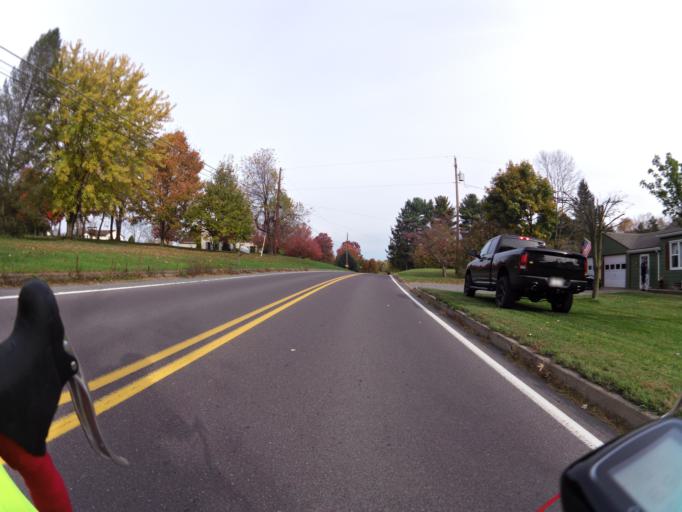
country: US
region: Pennsylvania
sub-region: Union County
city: New Columbia
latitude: 41.0461
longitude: -76.8827
